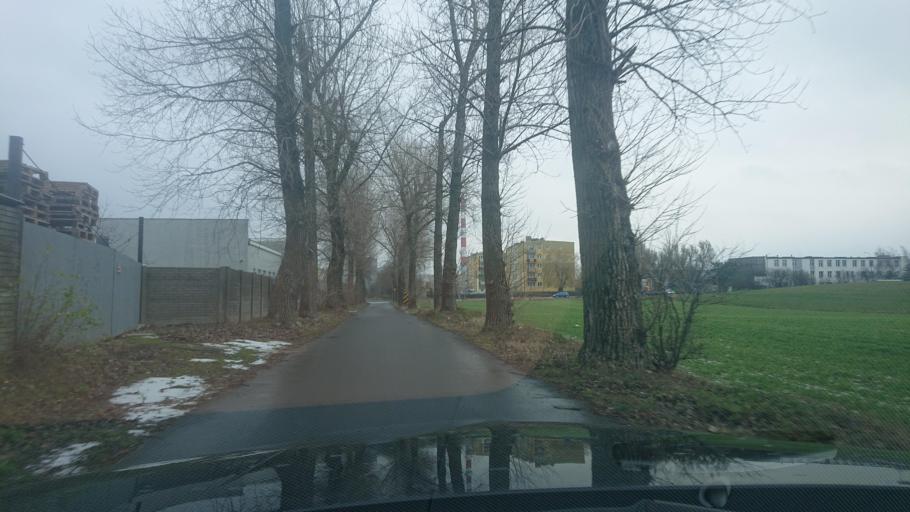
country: PL
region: Greater Poland Voivodeship
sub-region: Powiat gnieznienski
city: Gniezno
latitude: 52.5581
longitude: 17.6056
